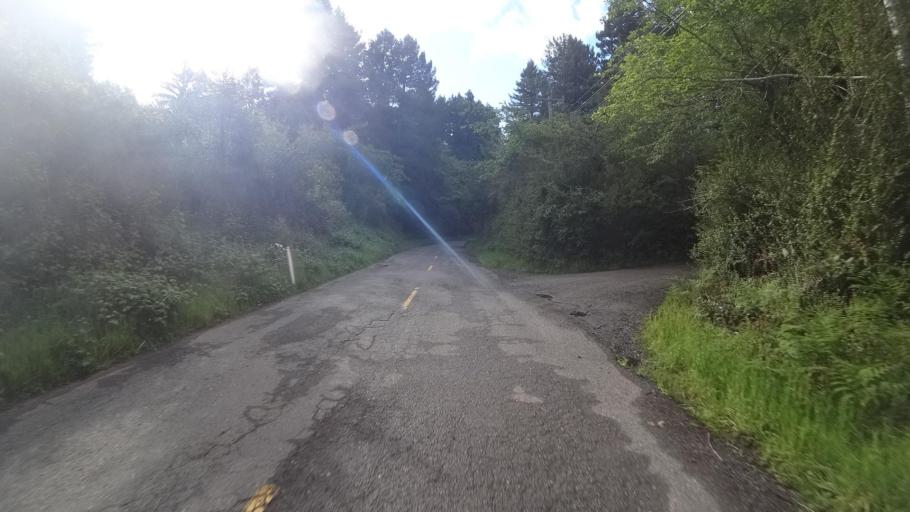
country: US
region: California
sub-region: Humboldt County
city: Westhaven-Moonstone
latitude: 41.0516
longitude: -124.1205
